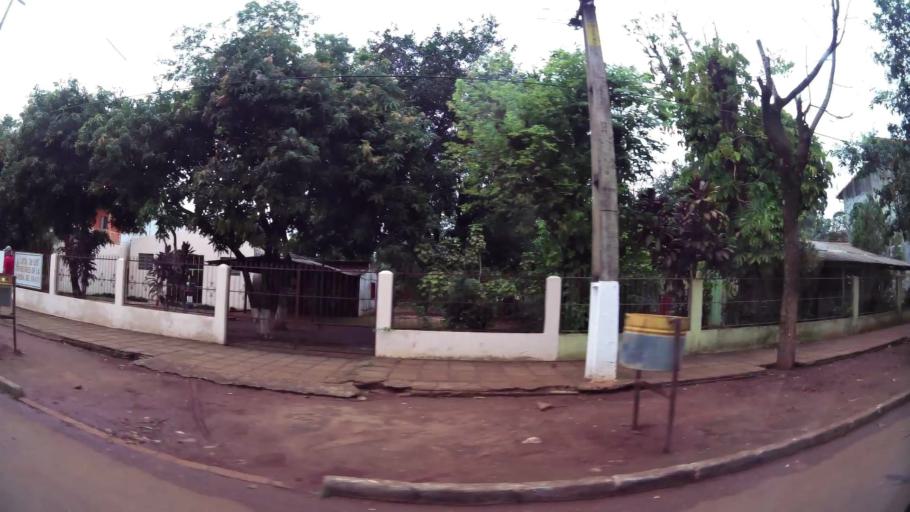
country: PY
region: Alto Parana
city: Ciudad del Este
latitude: -25.4823
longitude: -54.7603
